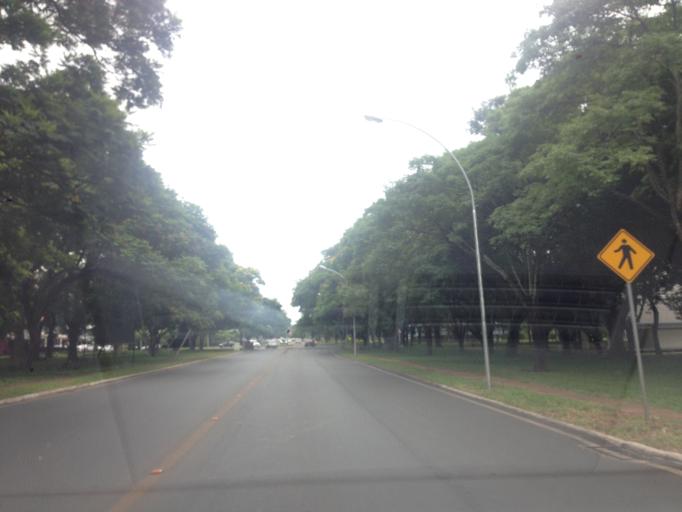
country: BR
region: Federal District
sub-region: Brasilia
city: Brasilia
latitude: -15.8212
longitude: -47.9125
